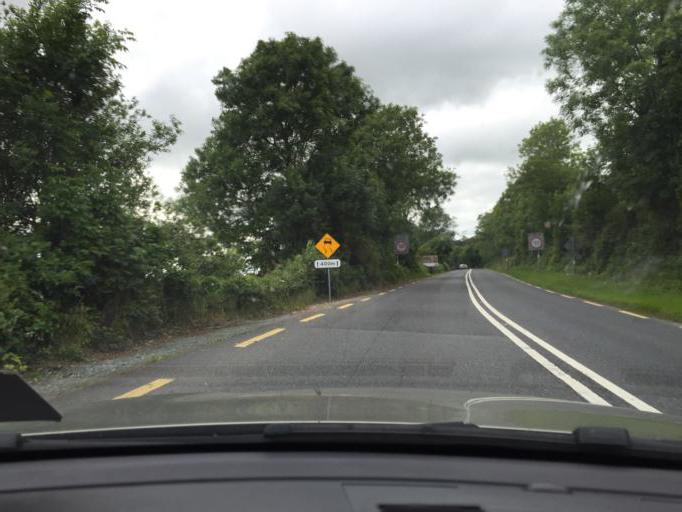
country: IE
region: Munster
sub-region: Waterford
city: Dungarvan
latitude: 52.1143
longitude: -7.5689
